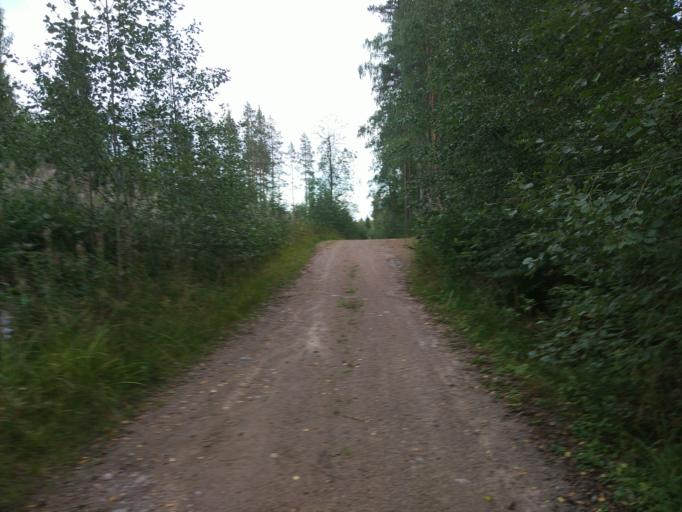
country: RU
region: Leningrad
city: Kuznechnoye
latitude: 61.1191
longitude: 29.5980
